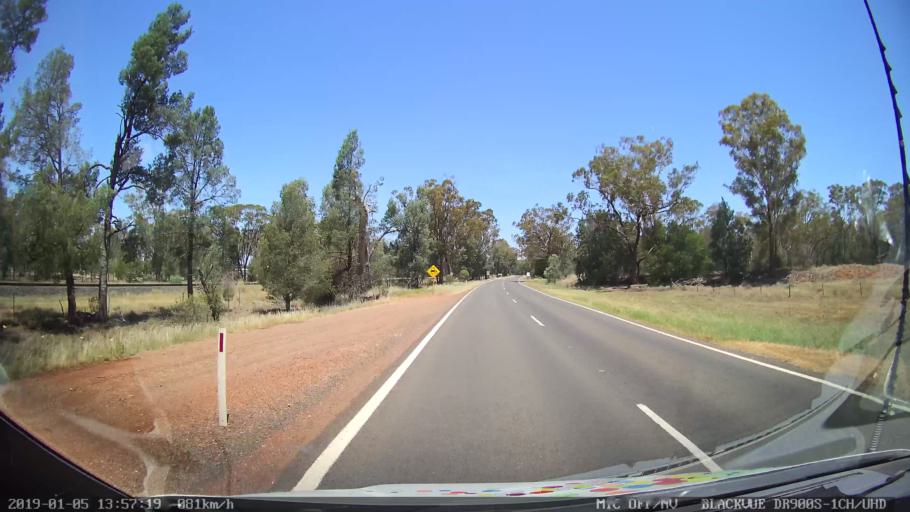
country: AU
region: New South Wales
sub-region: Gunnedah
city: Gunnedah
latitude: -31.1261
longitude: 150.2739
